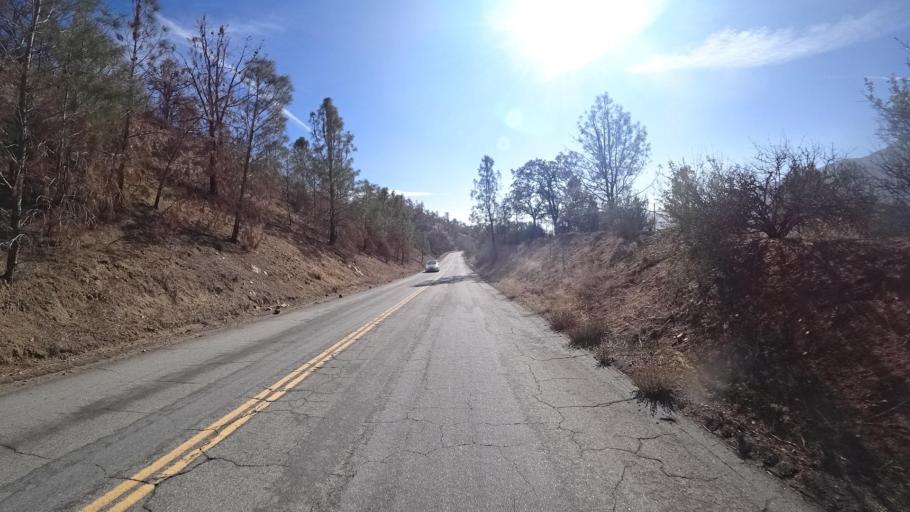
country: US
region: California
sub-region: Kern County
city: Bodfish
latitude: 35.4538
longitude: -118.5278
